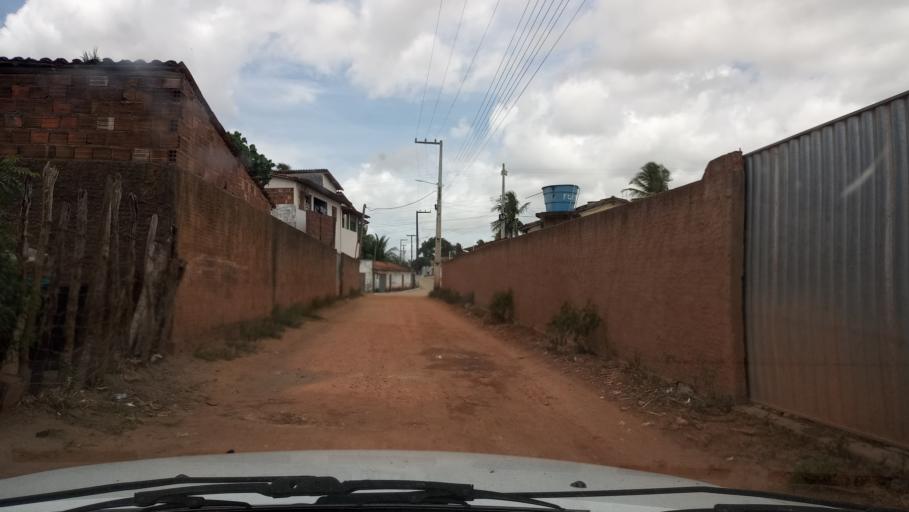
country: BR
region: Rio Grande do Norte
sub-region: Goianinha
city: Goianinha
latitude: -6.2927
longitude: -35.2807
